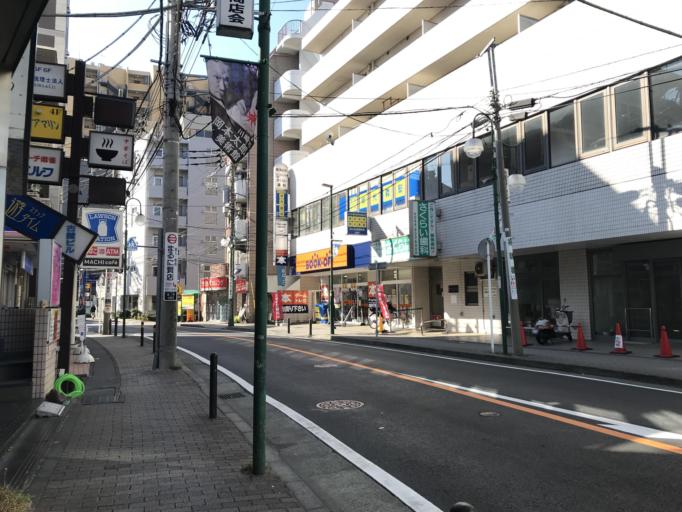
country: JP
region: Tokyo
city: Chofugaoka
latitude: 35.6176
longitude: 139.5660
